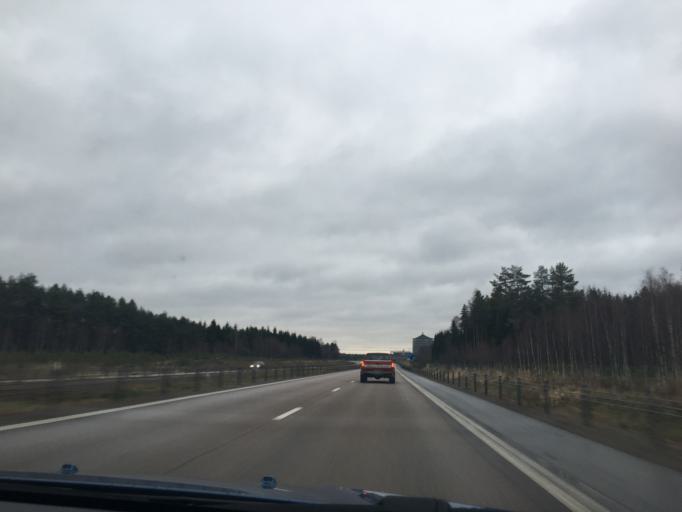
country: SE
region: Uppsala
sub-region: Alvkarleby Kommun
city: AElvkarleby
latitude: 60.4537
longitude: 17.4154
